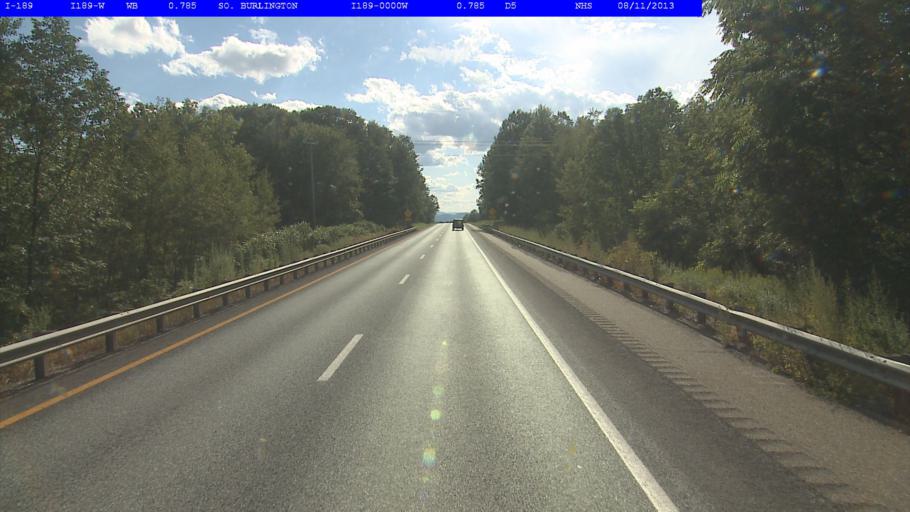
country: US
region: Vermont
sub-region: Chittenden County
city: South Burlington
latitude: 44.4505
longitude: -73.1947
